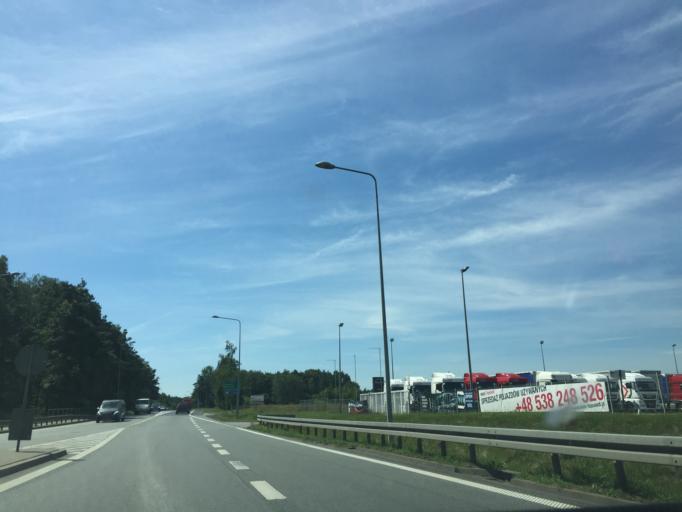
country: PL
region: Lodz Voivodeship
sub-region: Piotrkow Trybunalski
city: Piotrkow Trybunalski
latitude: 51.4407
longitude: 19.7219
